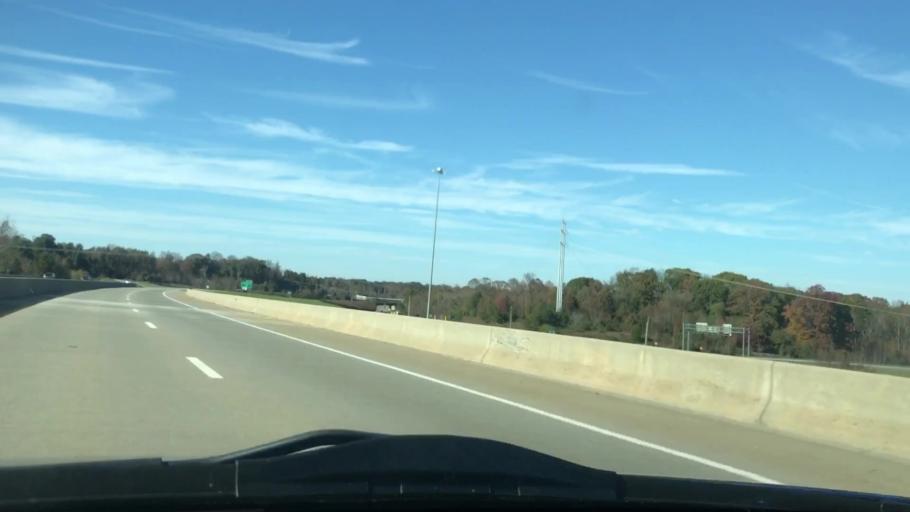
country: US
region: North Carolina
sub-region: Randolph County
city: Archdale
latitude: 35.9452
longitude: -79.9716
